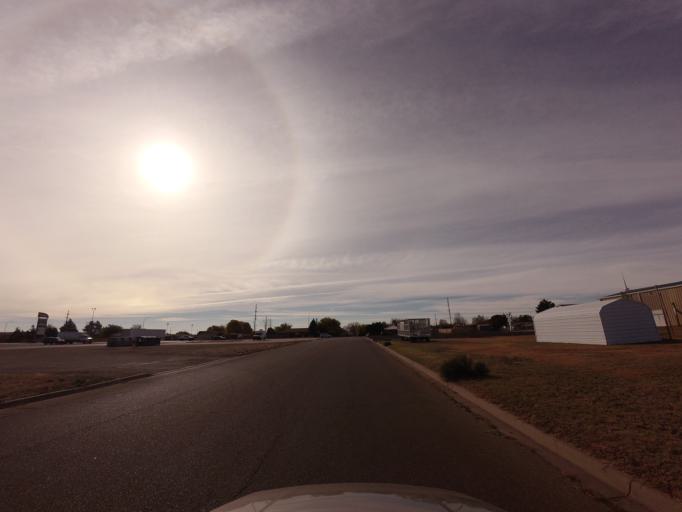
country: US
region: New Mexico
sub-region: Curry County
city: Clovis
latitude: 34.4204
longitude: -103.2210
